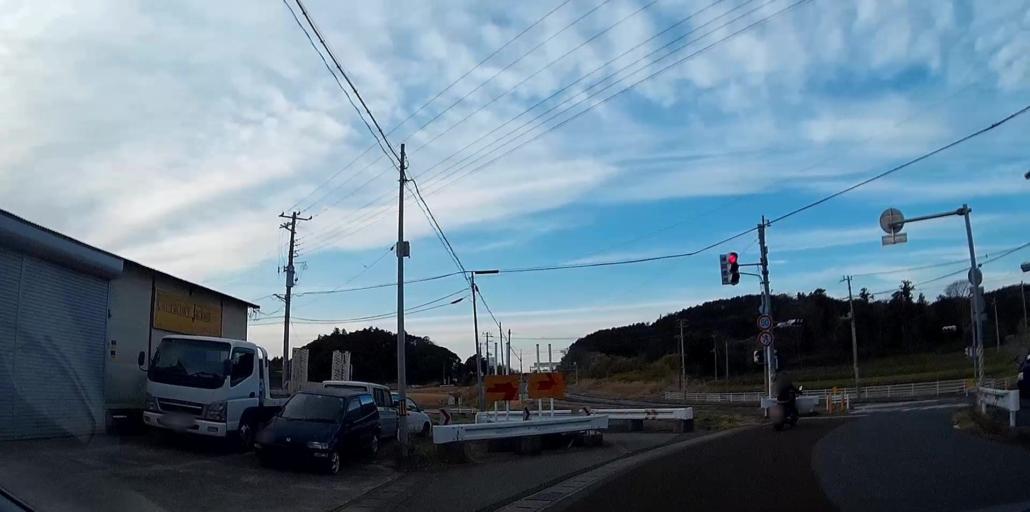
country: JP
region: Chiba
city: Ichihara
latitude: 35.3934
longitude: 140.0553
